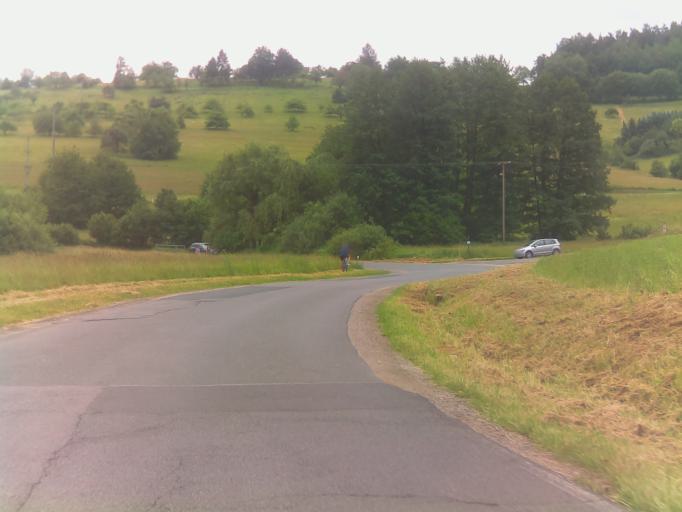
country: DE
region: Bavaria
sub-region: Regierungsbezirk Unterfranken
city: Johannesberg
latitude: 50.0538
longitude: 9.1345
